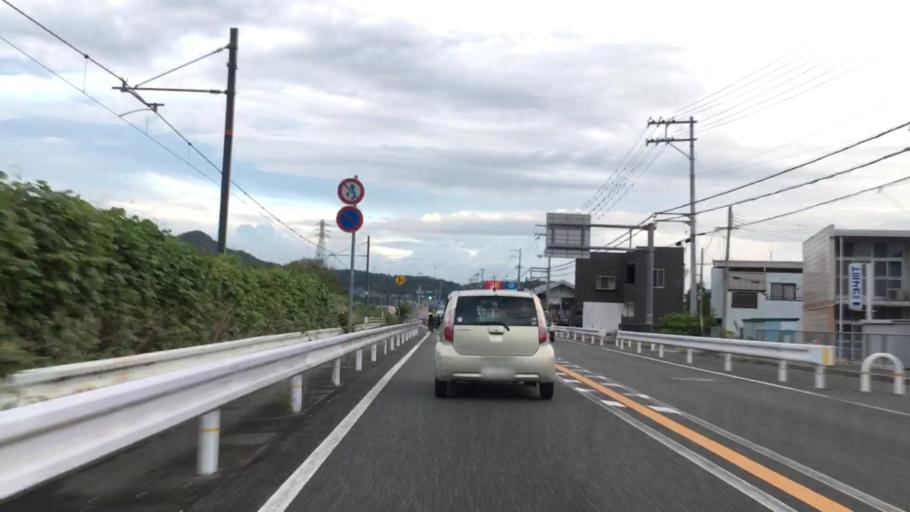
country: JP
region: Hyogo
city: Himeji
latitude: 34.8760
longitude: 134.7293
